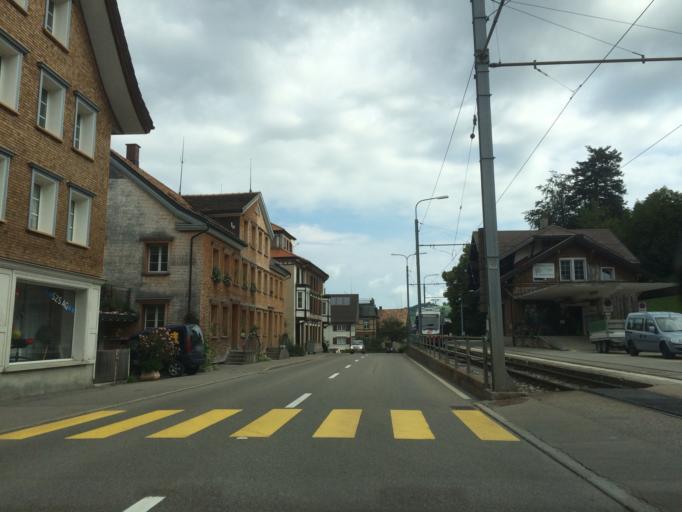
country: CH
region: Appenzell Ausserrhoden
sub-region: Bezirk Mittelland
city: Trogen
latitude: 47.4069
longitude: 9.4609
